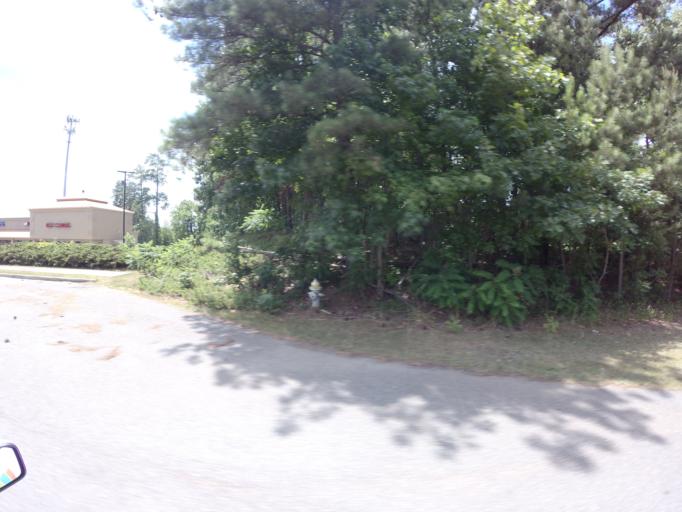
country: US
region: Georgia
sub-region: Fulton County
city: Johns Creek
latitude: 34.0722
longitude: -84.2035
